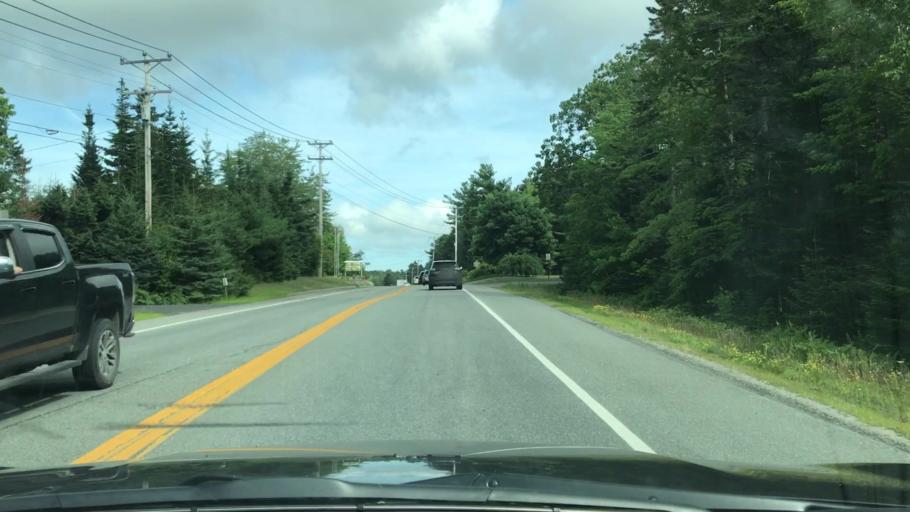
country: US
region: Maine
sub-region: Hancock County
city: Trenton
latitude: 44.4202
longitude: -68.3593
